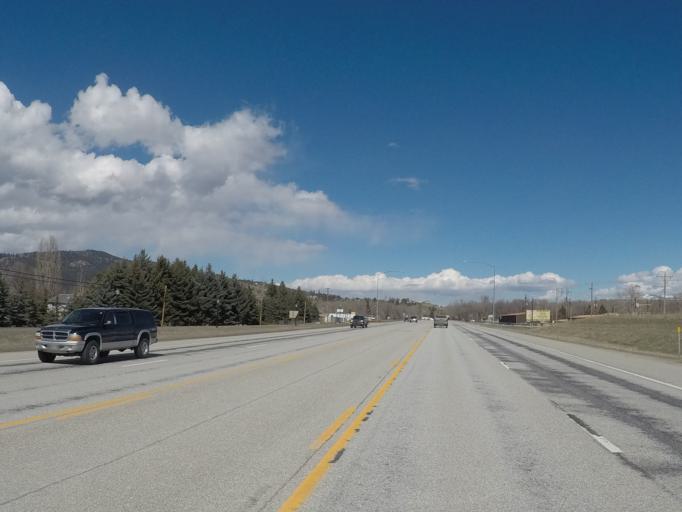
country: US
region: Montana
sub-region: Missoula County
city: Lolo
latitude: 46.7423
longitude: -114.0815
